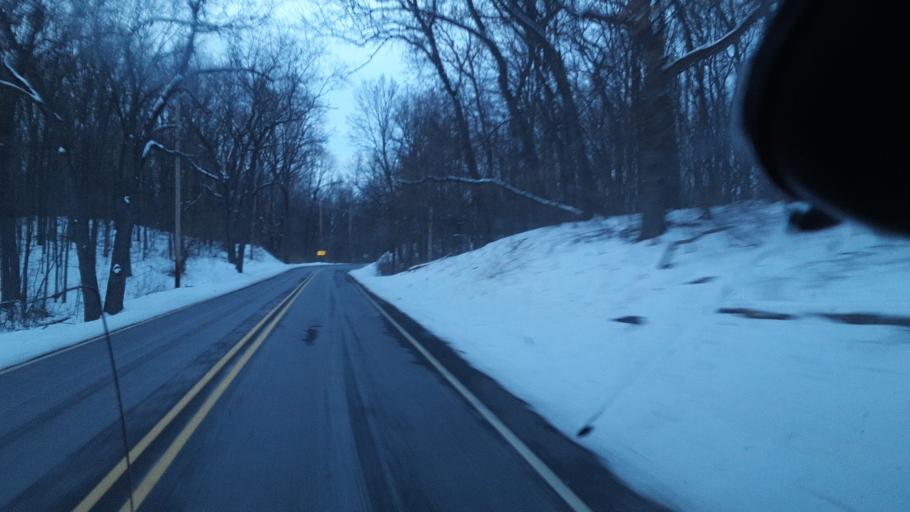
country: US
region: Michigan
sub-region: Jackson County
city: Grass Lake
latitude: 42.3052
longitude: -84.2092
